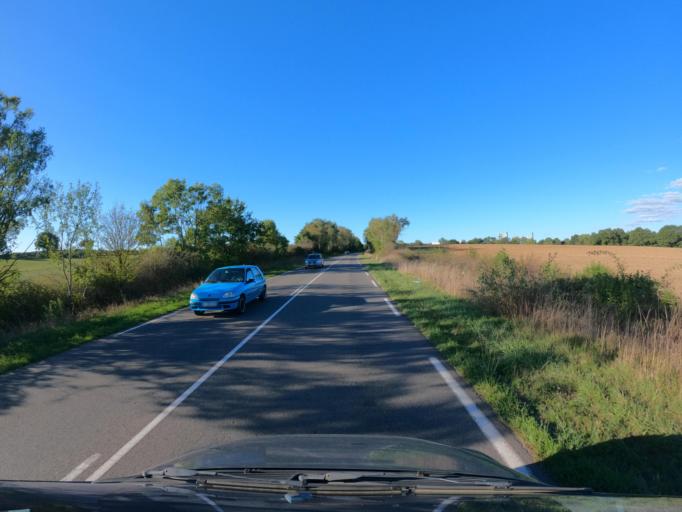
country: FR
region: Bourgogne
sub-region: Departement de Saone-et-Loire
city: Torcy
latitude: 46.7513
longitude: 4.4408
